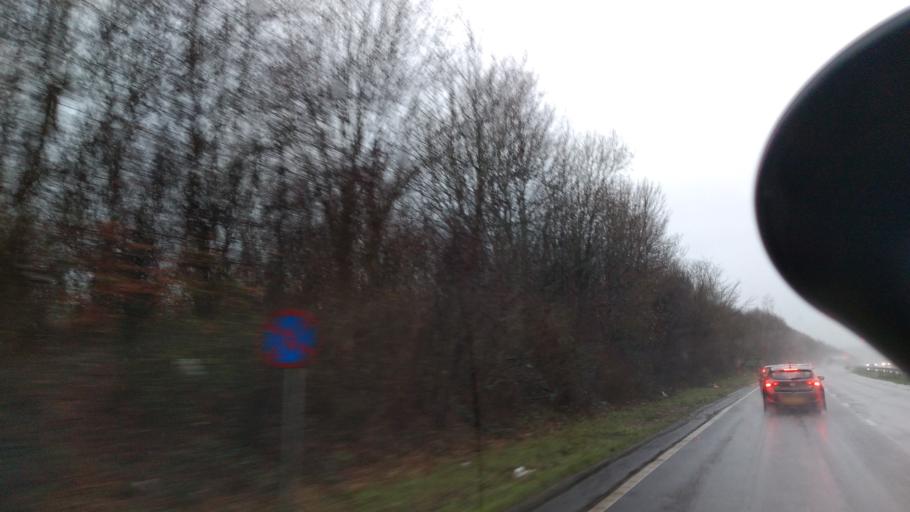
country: GB
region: England
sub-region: Brighton and Hove
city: Brighton
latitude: 50.8697
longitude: -0.1356
